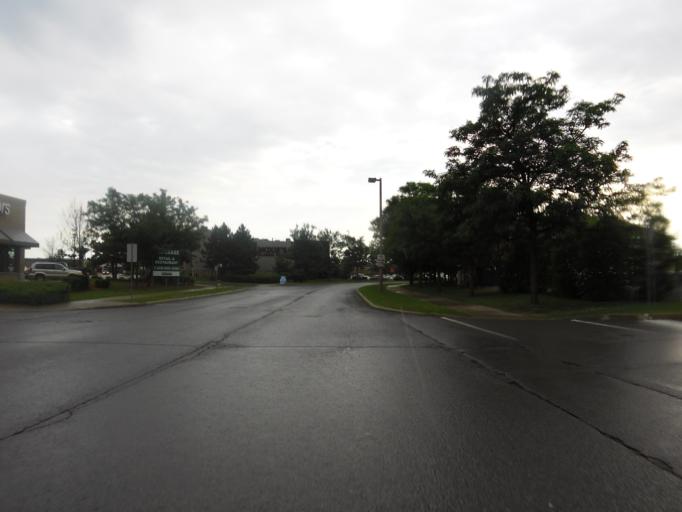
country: CA
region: Ontario
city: Bells Corners
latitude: 45.3105
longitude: -75.9117
